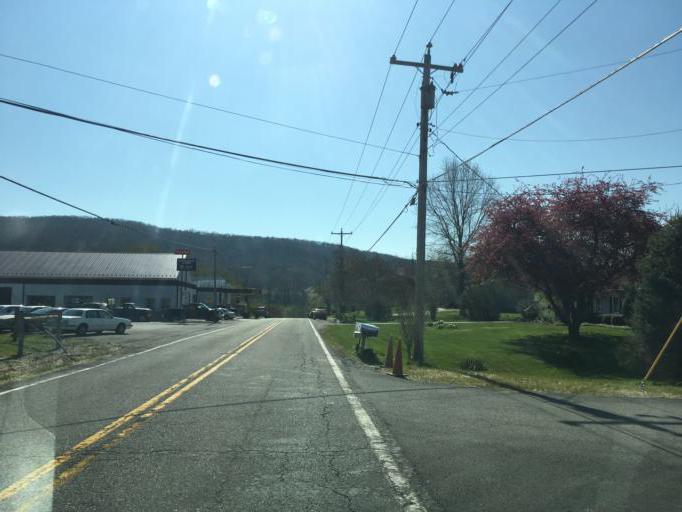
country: US
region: Maryland
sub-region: Frederick County
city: Myersville
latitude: 39.5650
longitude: -77.5290
